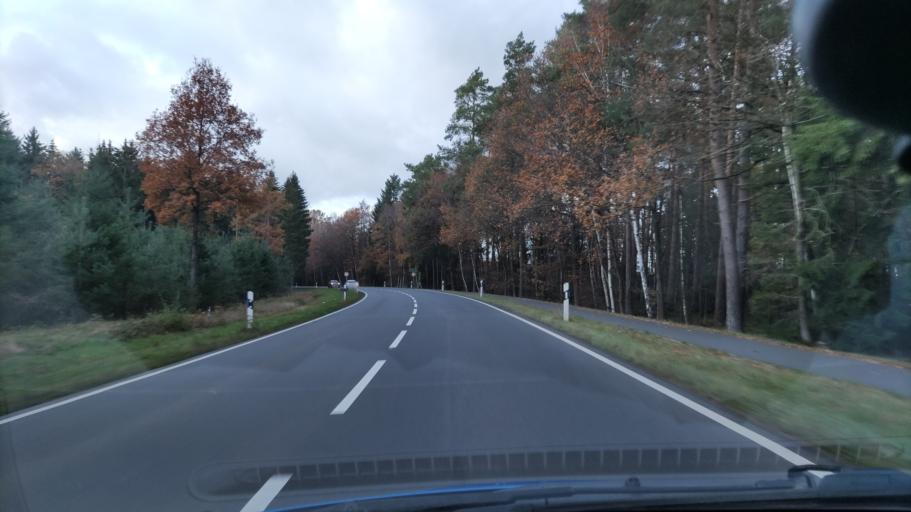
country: DE
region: Lower Saxony
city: Neuenkirchen
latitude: 53.0225
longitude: 9.7725
